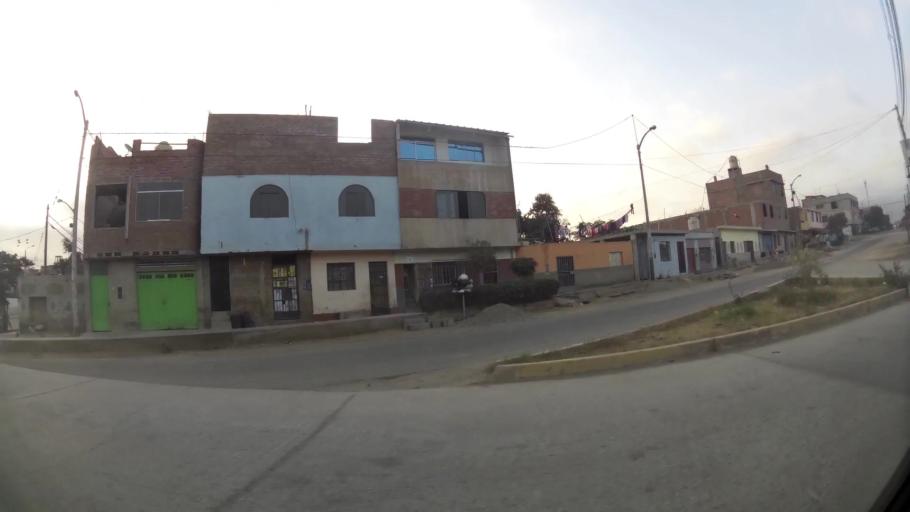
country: PE
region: La Libertad
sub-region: Provincia de Trujillo
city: El Porvenir
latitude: -8.0803
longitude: -79.0051
